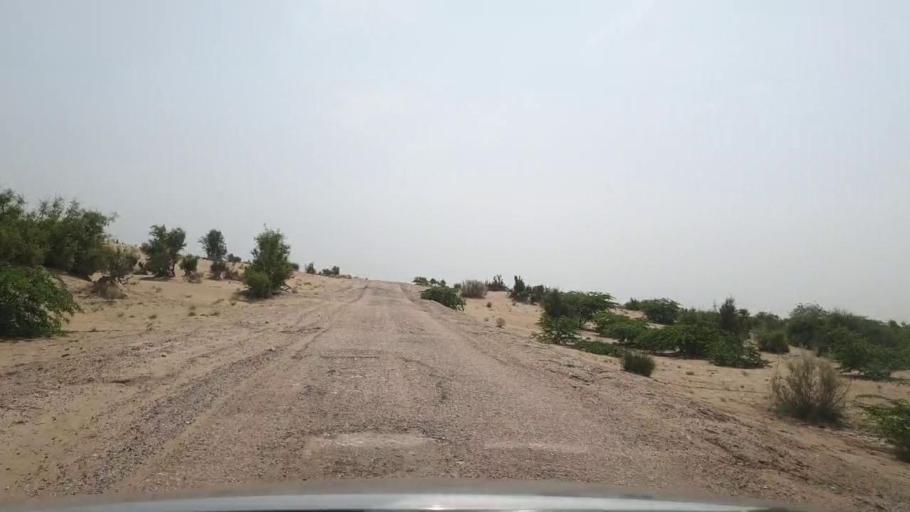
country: PK
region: Sindh
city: Pano Aqil
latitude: 27.6173
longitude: 69.1231
